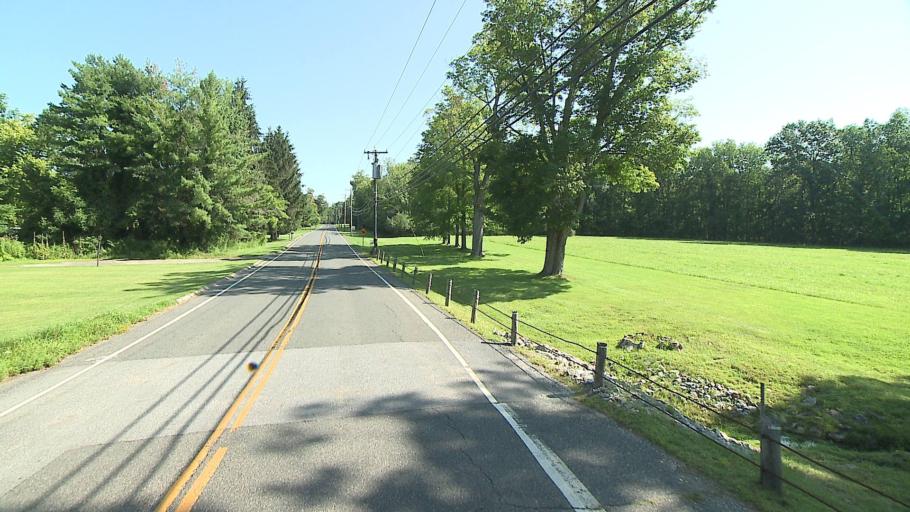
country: US
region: Connecticut
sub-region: Litchfield County
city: Kent
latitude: 41.8635
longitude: -73.4783
